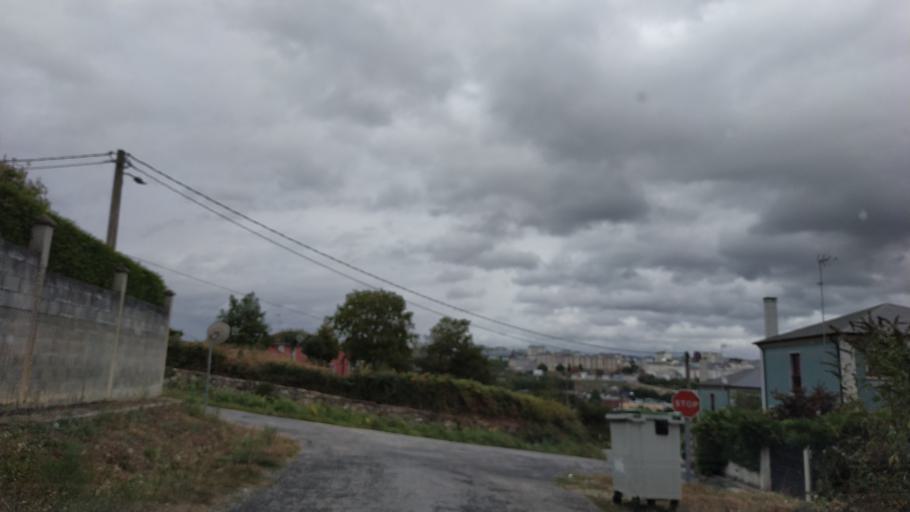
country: ES
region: Galicia
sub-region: Provincia de Lugo
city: Lugo
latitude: 42.9993
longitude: -7.5754
